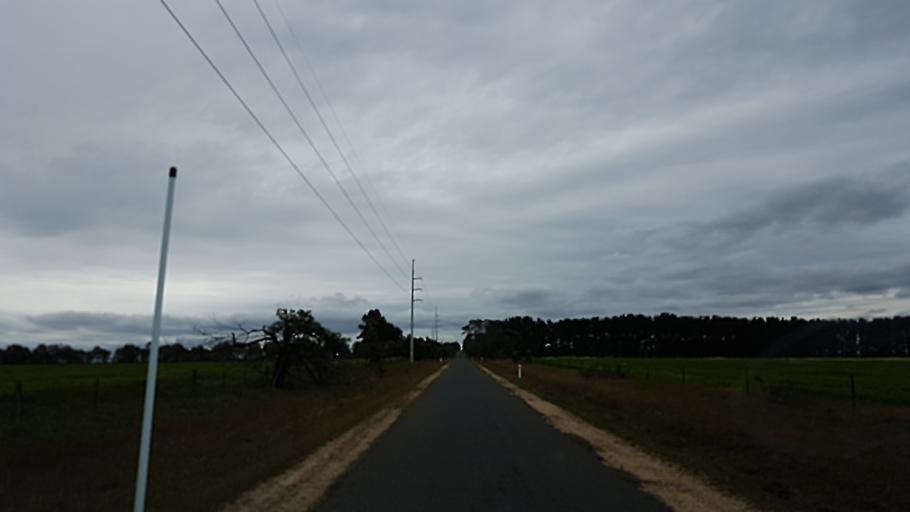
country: AU
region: Victoria
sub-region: Ballarat North
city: Mount Clear
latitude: -37.7794
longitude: 143.9803
